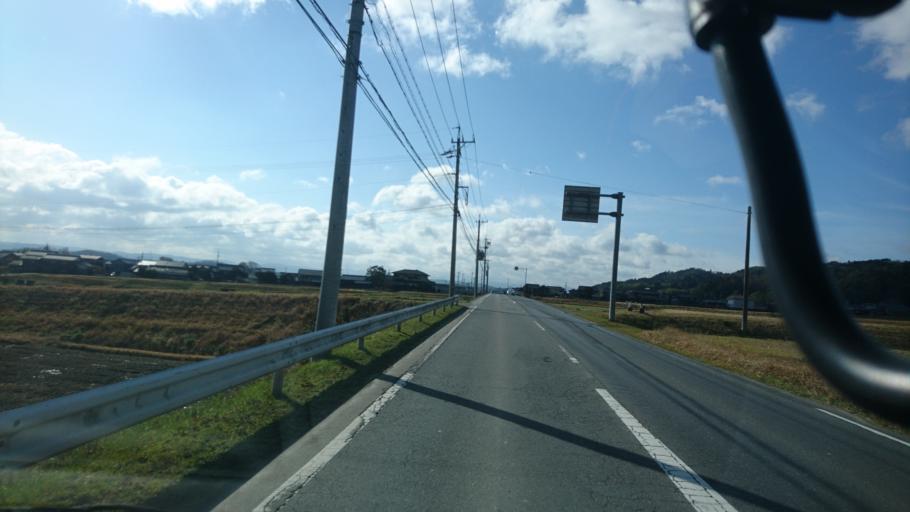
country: JP
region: Mie
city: Ueno-ebisumachi
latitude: 34.7697
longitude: 136.1072
